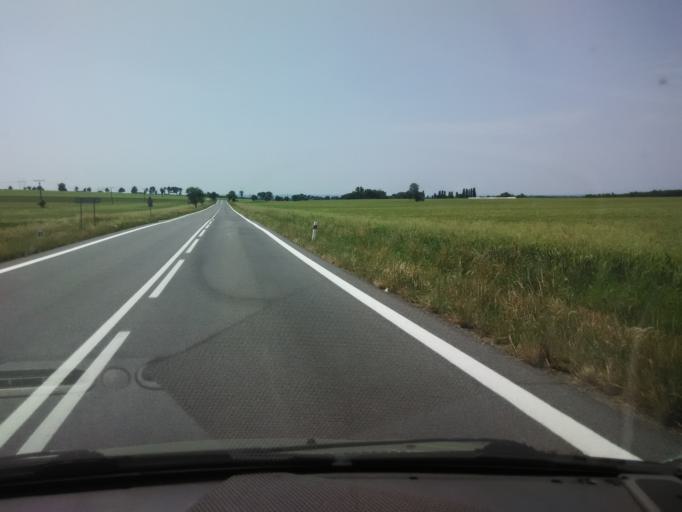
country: SK
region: Nitriansky
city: Levice
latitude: 48.2445
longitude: 18.6799
